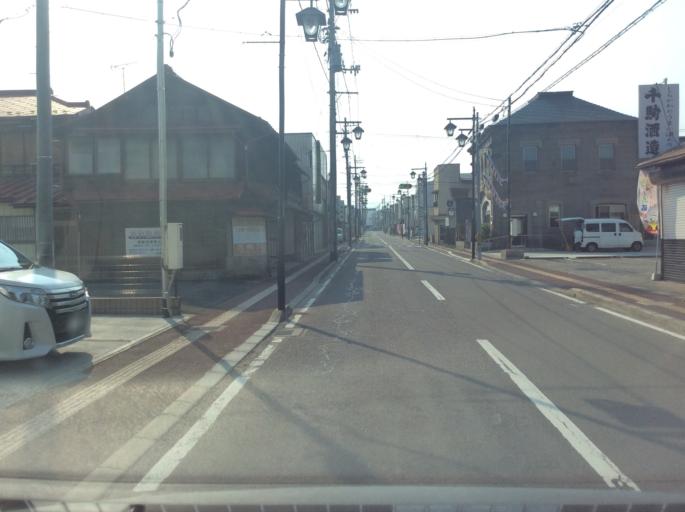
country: JP
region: Fukushima
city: Sukagawa
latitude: 37.1249
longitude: 140.2208
